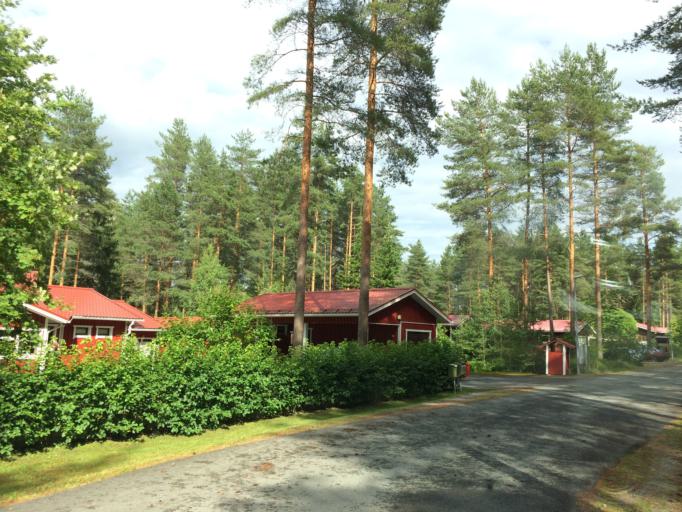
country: FI
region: Haeme
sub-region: Haemeenlinna
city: Turenki
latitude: 60.9408
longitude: 24.6425
